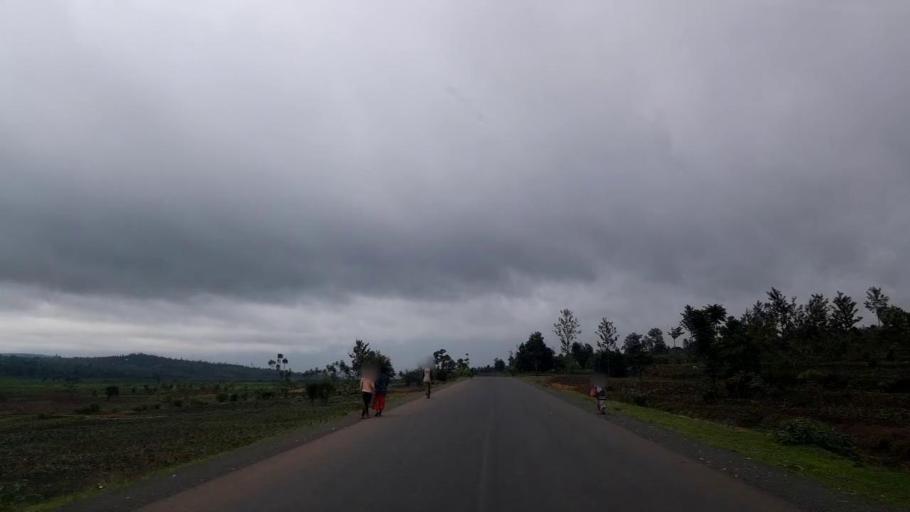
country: RW
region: Northern Province
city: Byumba
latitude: -1.4400
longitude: 30.2550
